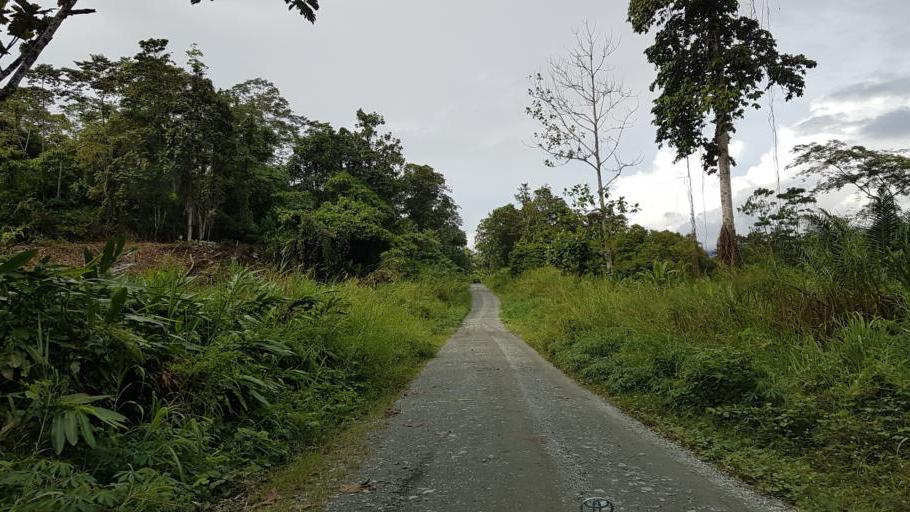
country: PG
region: Northern Province
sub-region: Sohe
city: Kokoda
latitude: -8.8869
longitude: 147.9900
